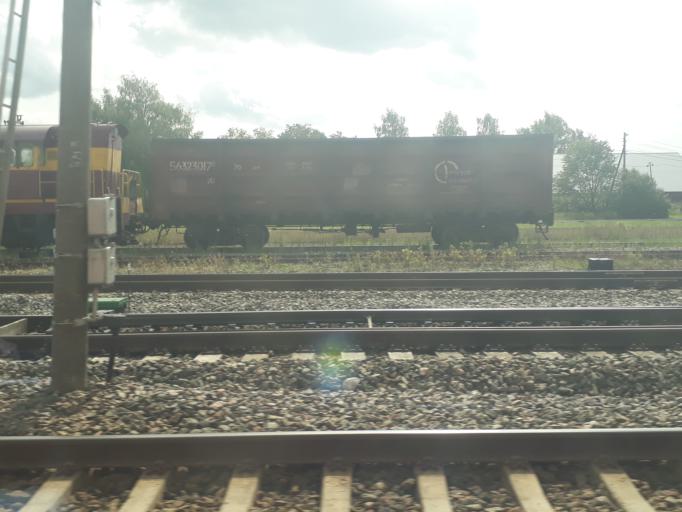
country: EE
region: Laeaene-Virumaa
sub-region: Tapa vald
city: Tapa
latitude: 59.2646
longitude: 25.9480
